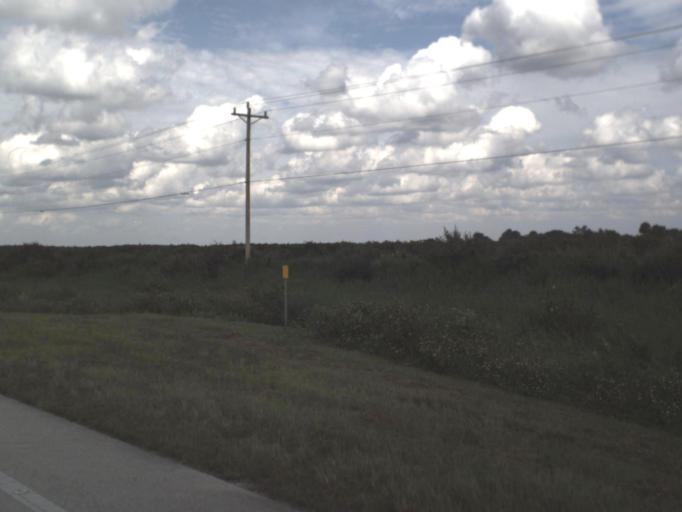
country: US
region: Florida
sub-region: Collier County
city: Immokalee
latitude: 26.5022
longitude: -81.4349
